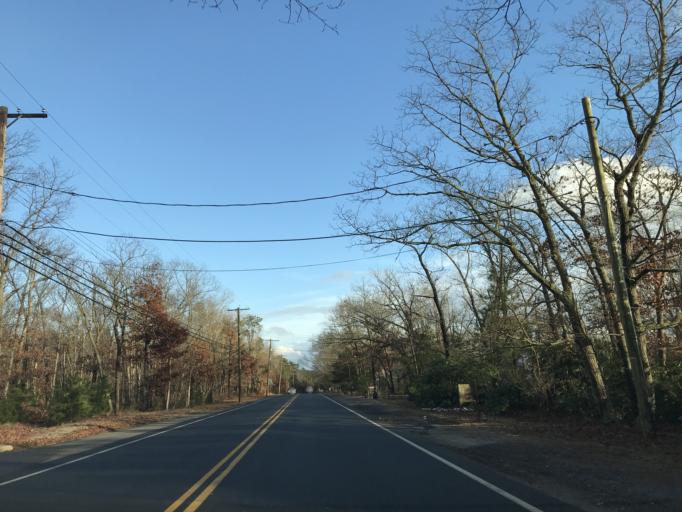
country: US
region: New Jersey
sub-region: Ocean County
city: Waretown
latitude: 39.7943
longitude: -74.2274
